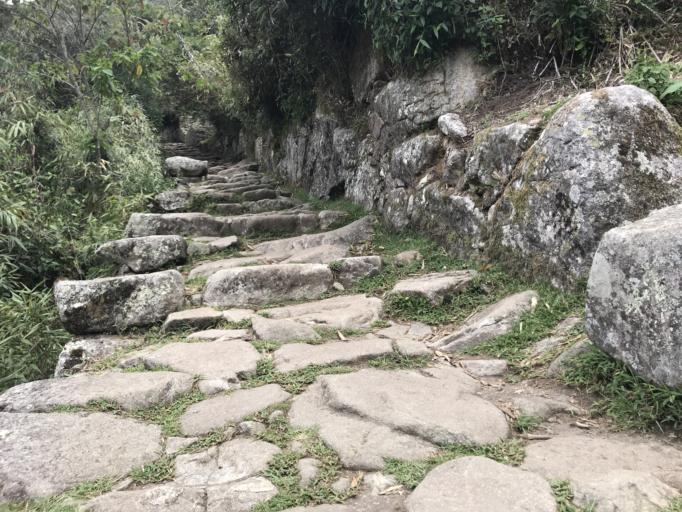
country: PE
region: Cusco
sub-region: Provincia de La Convencion
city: Santa Teresa
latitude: -13.1675
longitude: -72.5433
